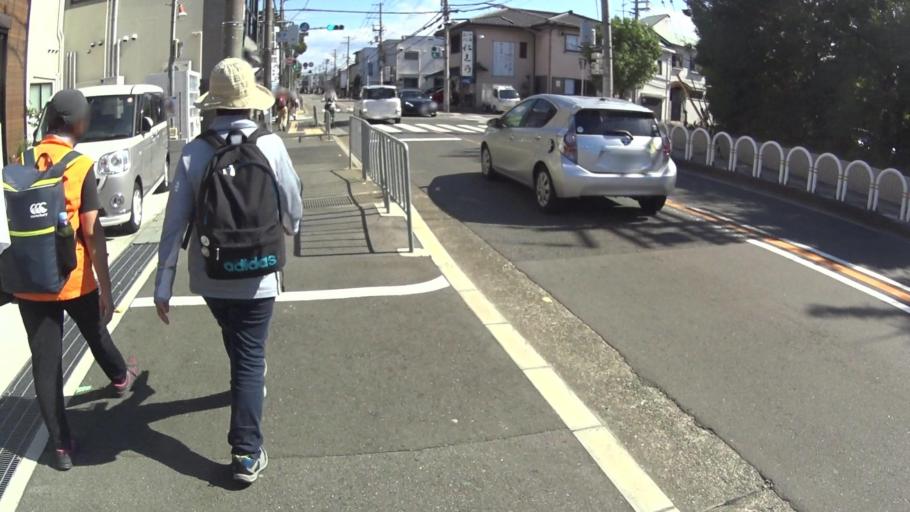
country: JP
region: Ehime
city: Kihoku-cho
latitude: 33.3816
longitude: 132.8232
